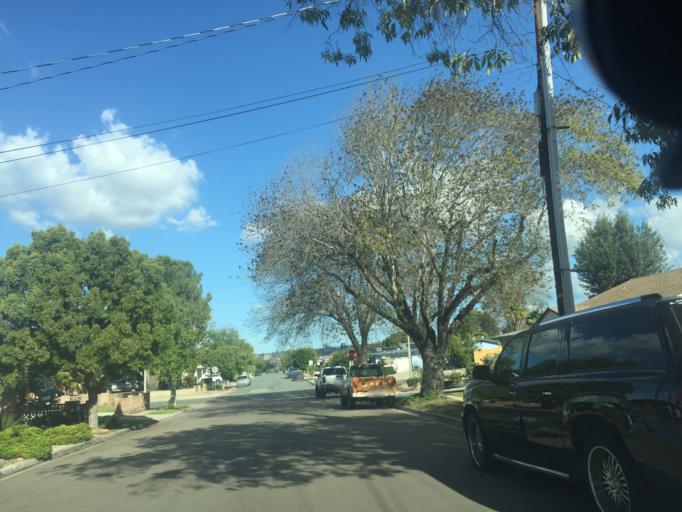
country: US
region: California
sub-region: San Diego County
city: La Mesa
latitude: 32.7924
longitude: -117.0889
